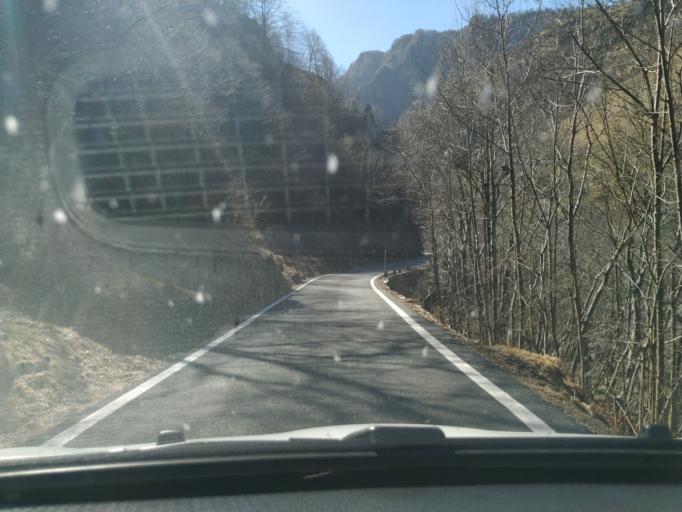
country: IT
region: Piedmont
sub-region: Provincia di Vercelli
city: Cervatto
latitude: 45.8861
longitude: 8.1784
